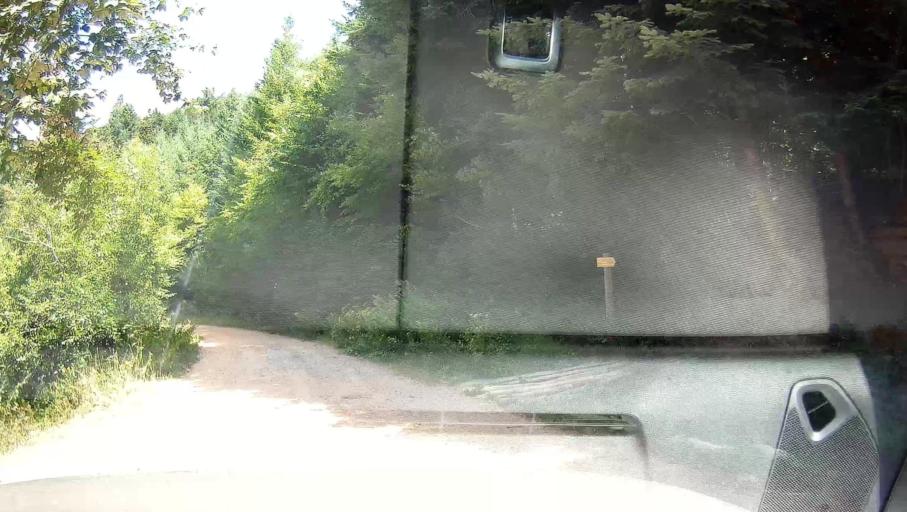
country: FR
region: Rhone-Alpes
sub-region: Departement du Rhone
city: Le Perreon
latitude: 46.0167
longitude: 4.5452
